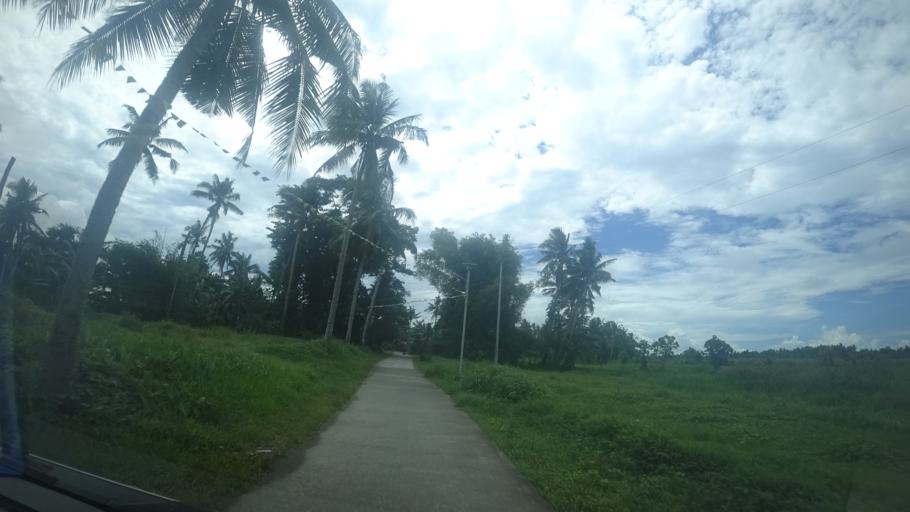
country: PH
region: Eastern Visayas
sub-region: Province of Leyte
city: MacArthur
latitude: 10.8318
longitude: 124.9924
